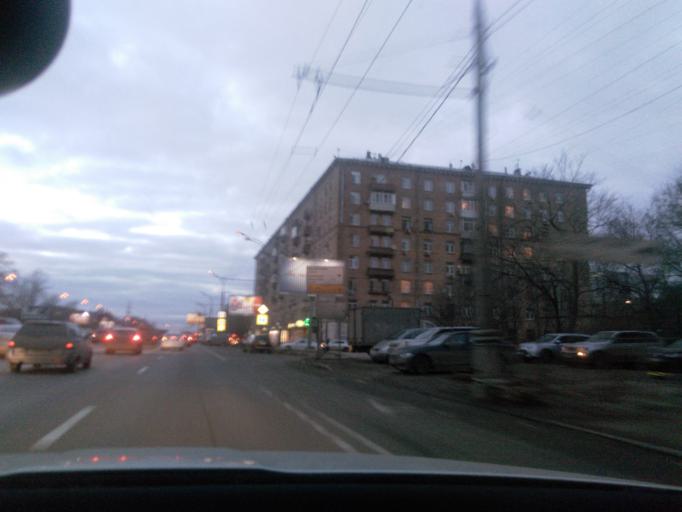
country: RU
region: Moskovskaya
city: Levoberezhnyy
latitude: 55.8325
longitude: 37.4871
